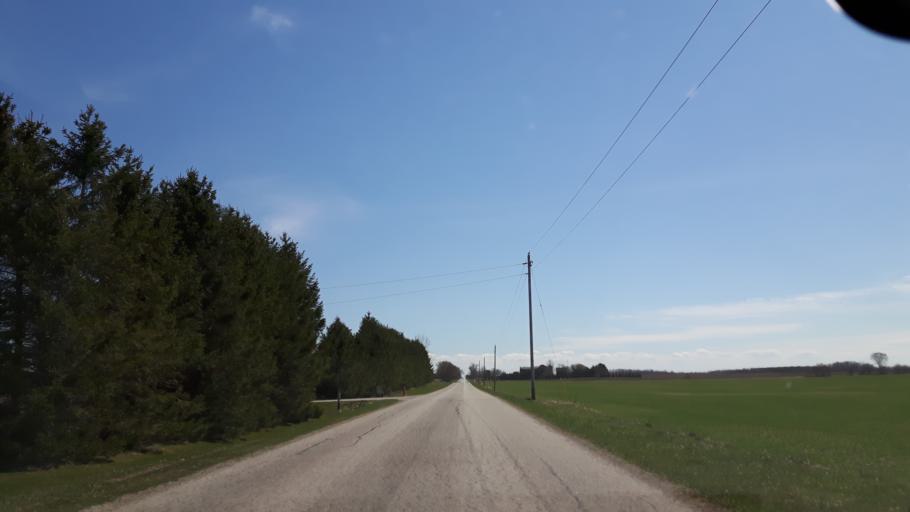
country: CA
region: Ontario
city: Goderich
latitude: 43.6397
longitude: -81.6440
